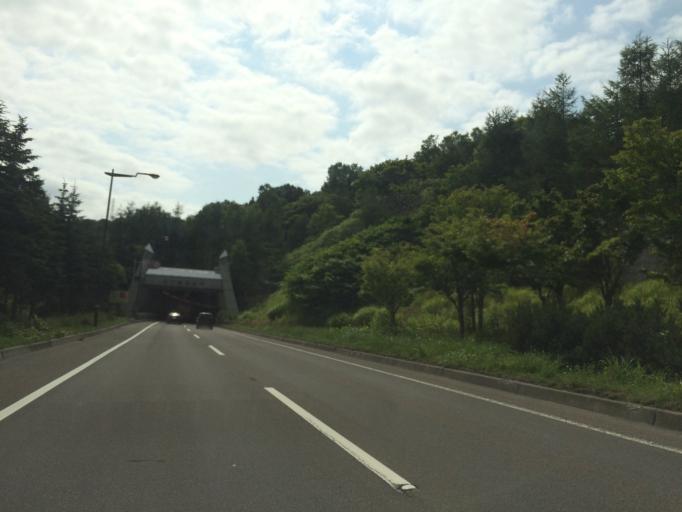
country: JP
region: Hokkaido
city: Otaru
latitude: 43.2067
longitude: 140.9744
